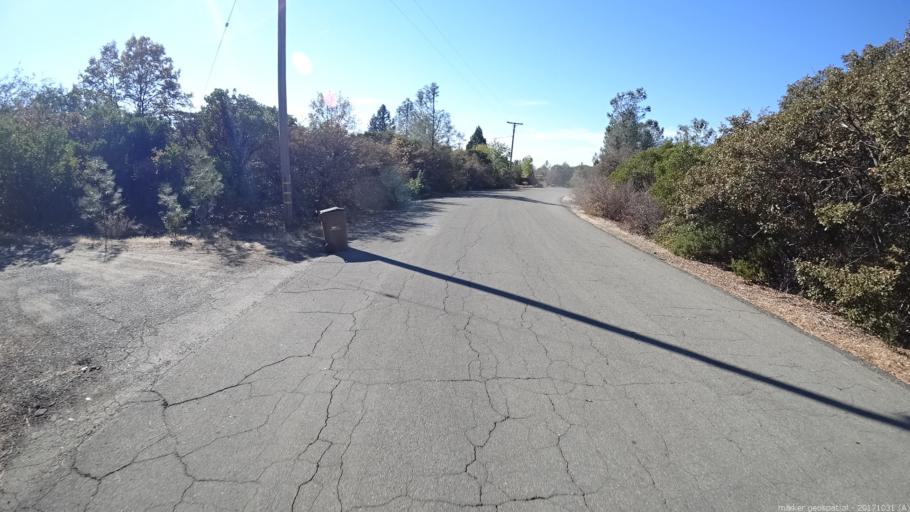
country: US
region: California
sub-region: Shasta County
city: Shingletown
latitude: 40.5080
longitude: -122.0156
